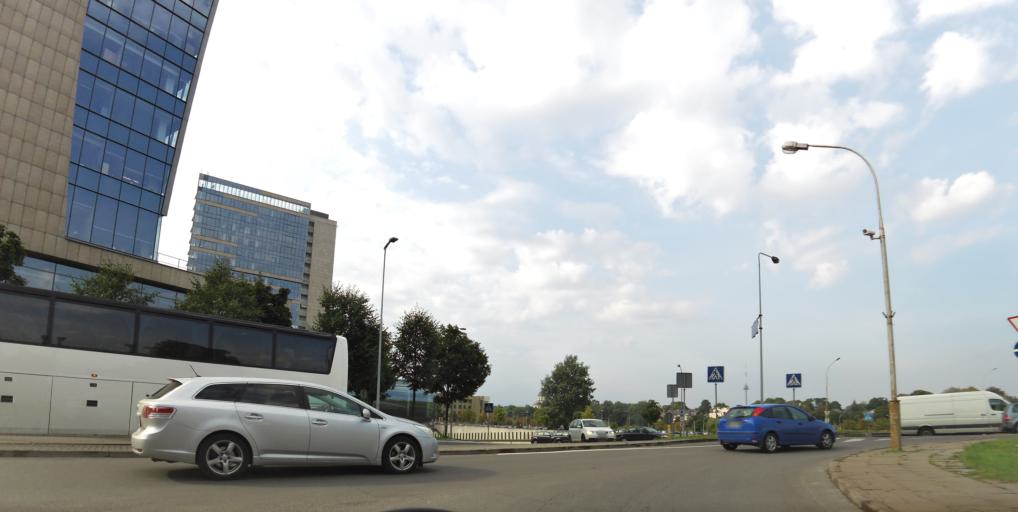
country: LT
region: Vilnius County
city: Naujamiestis
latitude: 54.6937
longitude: 25.2646
